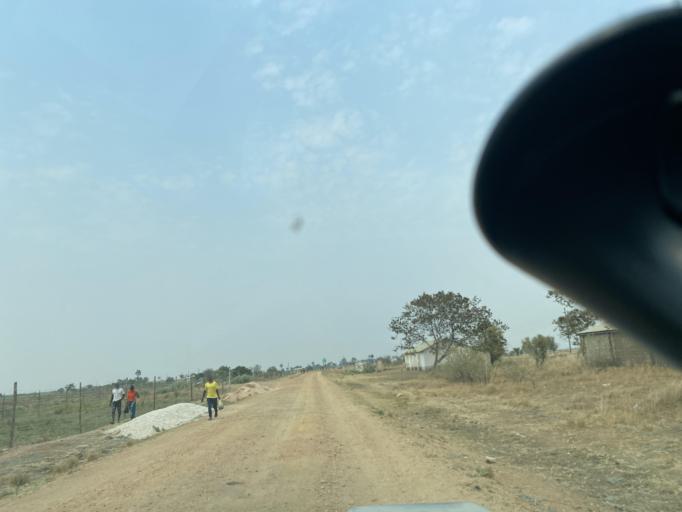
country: ZM
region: Lusaka
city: Kafue
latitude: -15.6840
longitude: 28.0092
